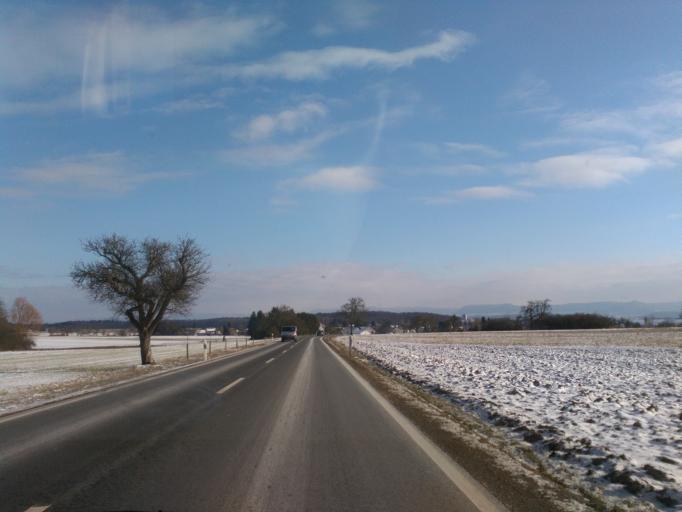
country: DE
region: Baden-Wuerttemberg
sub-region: Regierungsbezirk Stuttgart
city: Wolfschlugen
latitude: 48.6620
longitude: 9.2769
